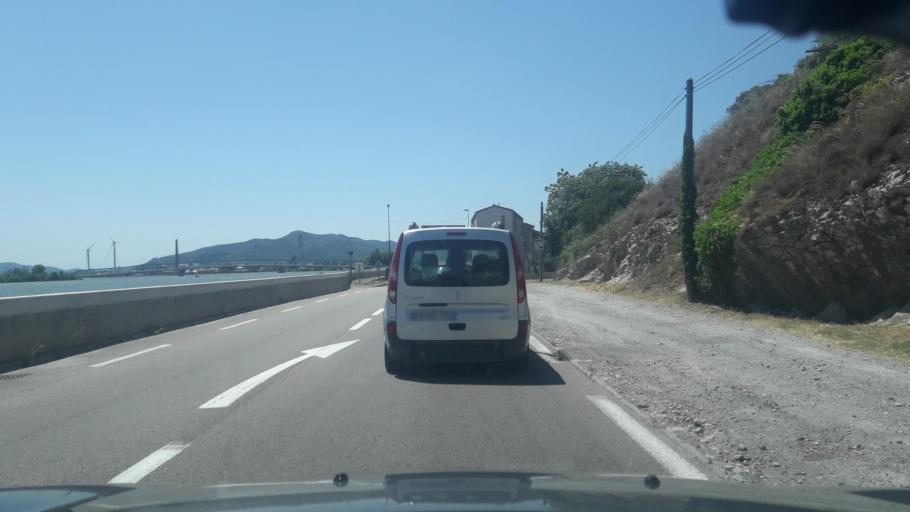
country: FR
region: Rhone-Alpes
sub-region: Departement de l'Ardeche
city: Le Pouzin
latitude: 44.7632
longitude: 4.7522
